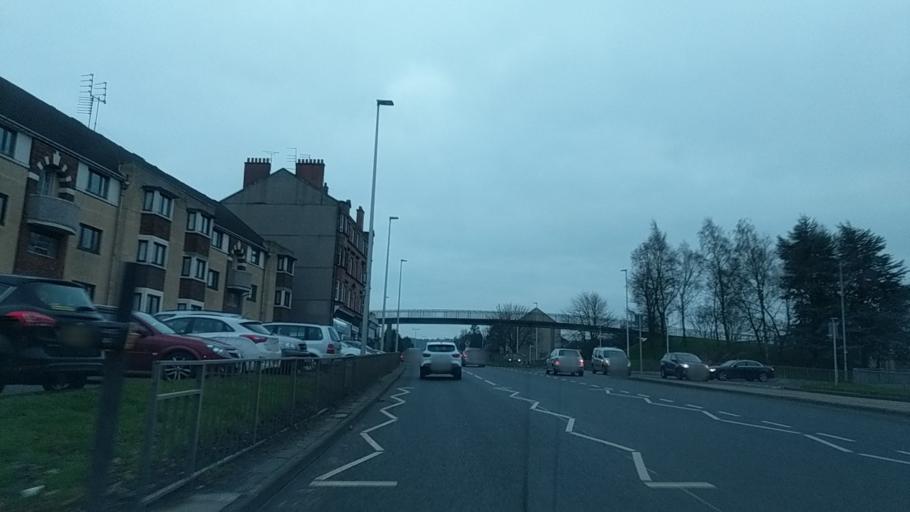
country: GB
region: Scotland
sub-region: South Lanarkshire
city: Rutherglen
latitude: 55.8263
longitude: -4.2180
